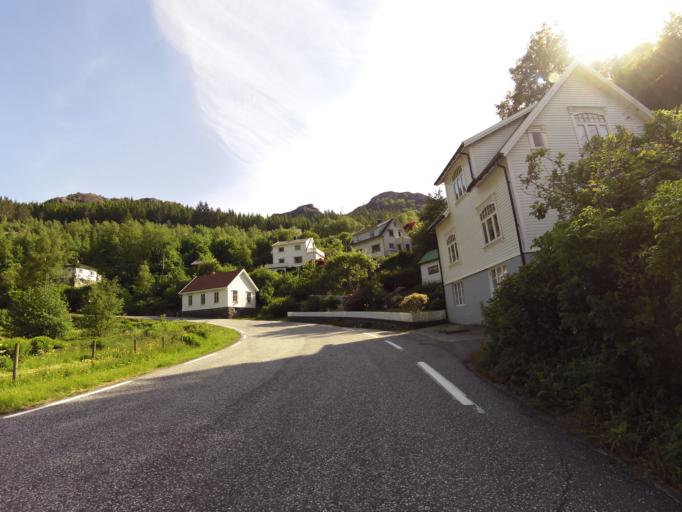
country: NO
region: Rogaland
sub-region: Sokndal
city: Hauge i Dalane
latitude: 58.3162
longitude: 6.3449
